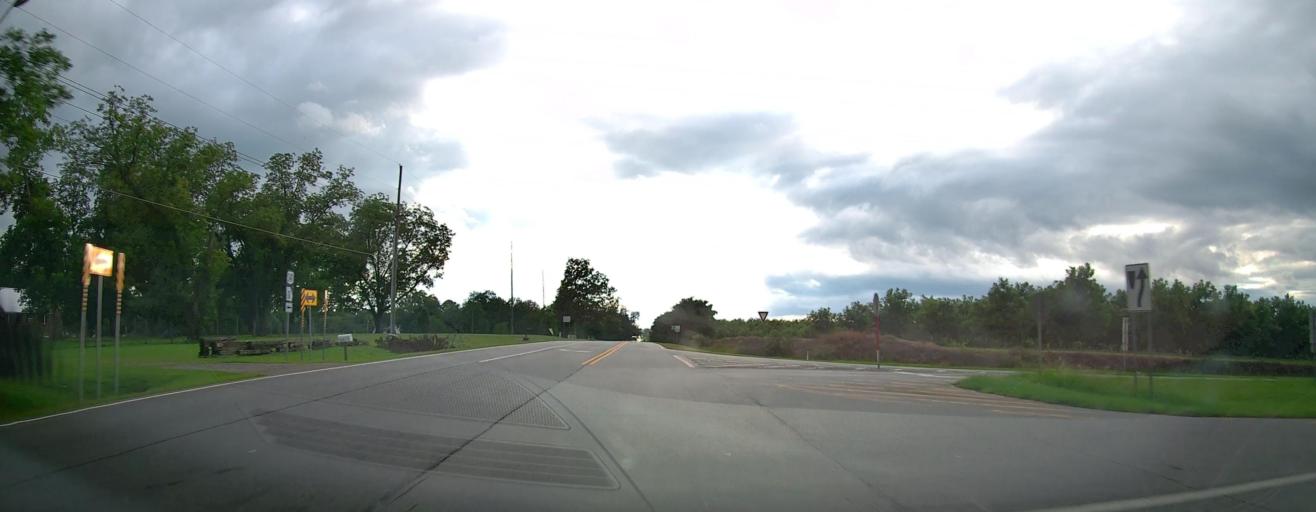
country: US
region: Georgia
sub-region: Houston County
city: Perry
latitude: 32.4546
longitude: -83.6929
